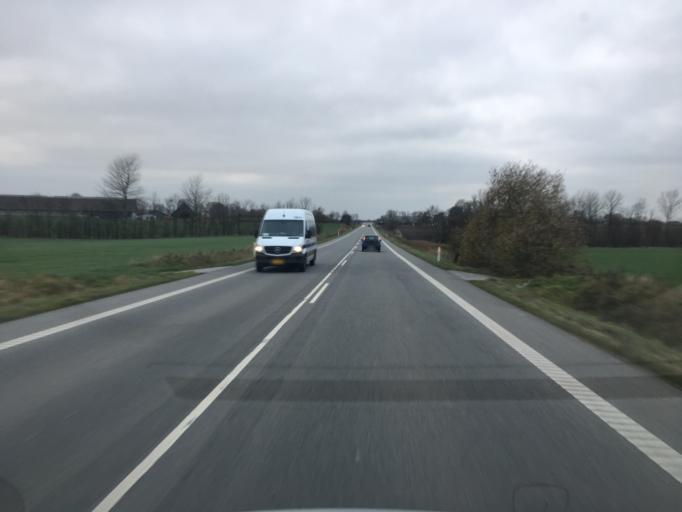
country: DK
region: South Denmark
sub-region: Aabenraa Kommune
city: Rodekro
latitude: 55.0259
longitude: 9.3550
